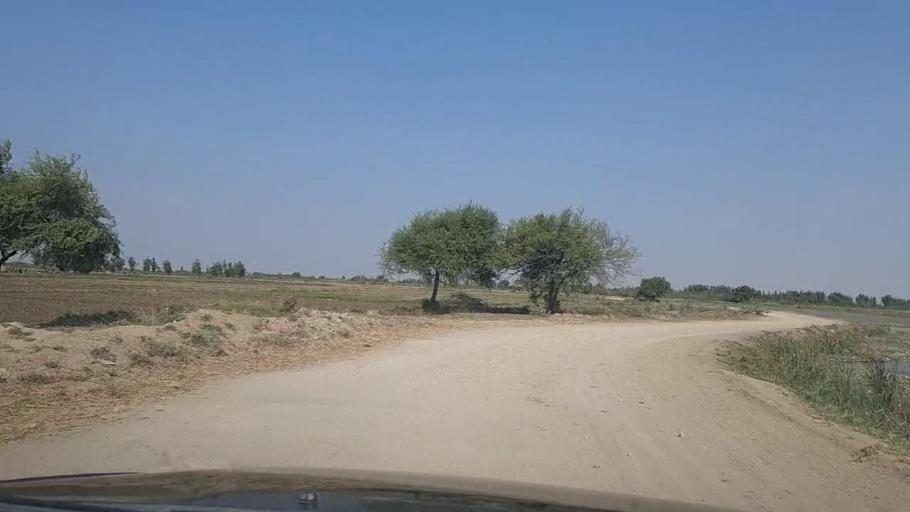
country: PK
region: Sindh
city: Thatta
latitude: 24.6268
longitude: 67.8137
